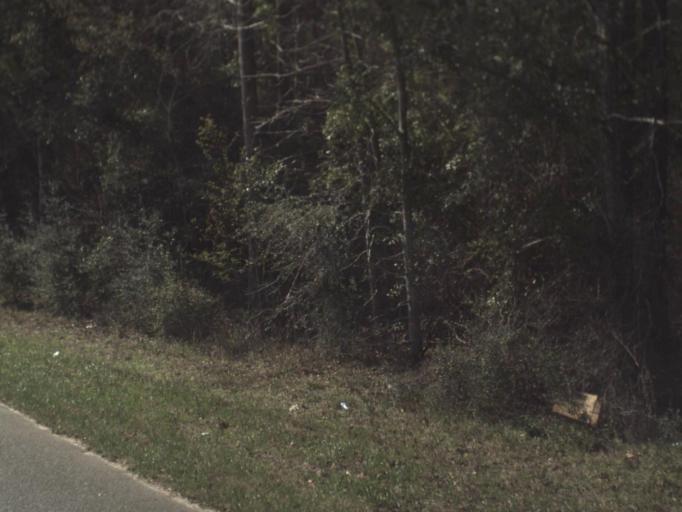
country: US
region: Florida
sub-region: Jackson County
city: Marianna
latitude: 30.6506
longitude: -85.1600
